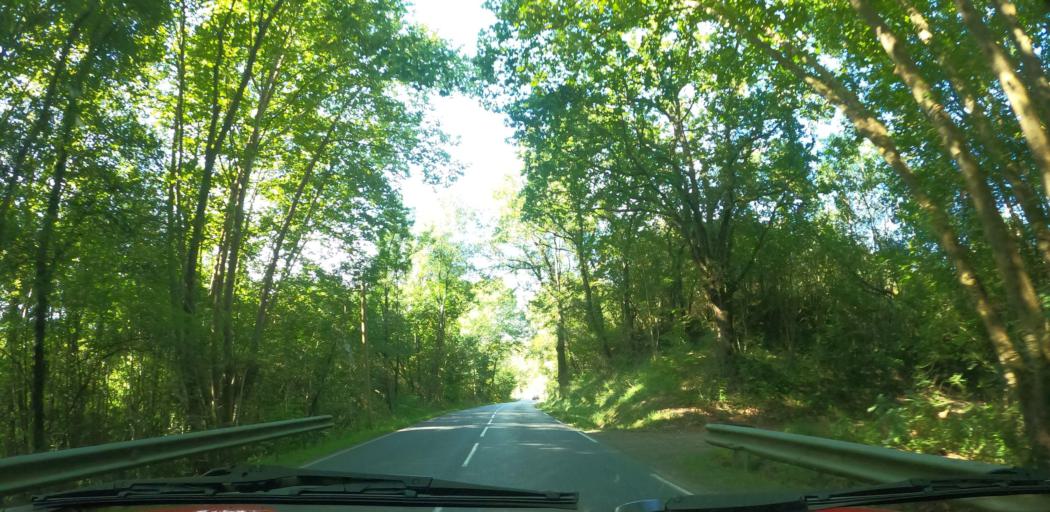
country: FR
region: Aquitaine
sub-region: Departement des Pyrenees-Atlantiques
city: Saint-Pee-sur-Nivelle
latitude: 43.3751
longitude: -1.5447
